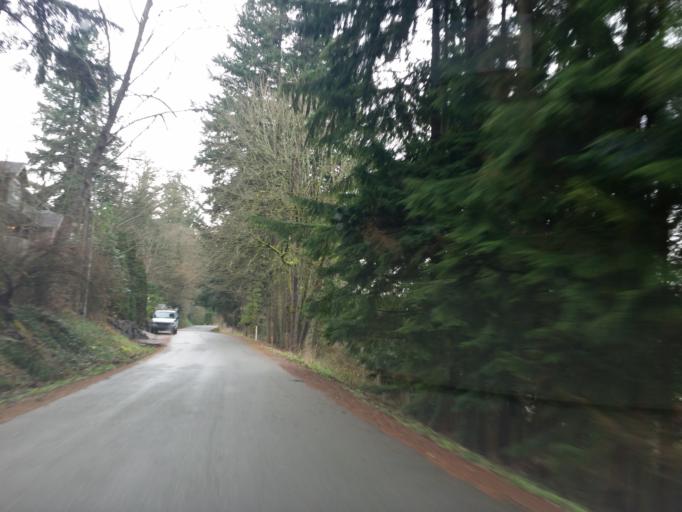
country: US
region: Washington
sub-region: King County
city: Shoreline
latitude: 47.7540
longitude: -122.3571
